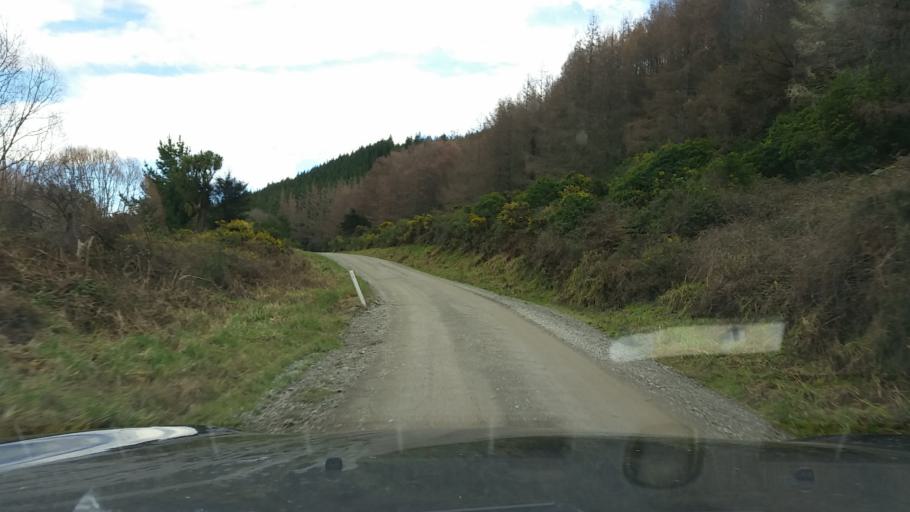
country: NZ
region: Nelson
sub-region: Nelson City
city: Nelson
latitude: -41.5771
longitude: 173.4354
